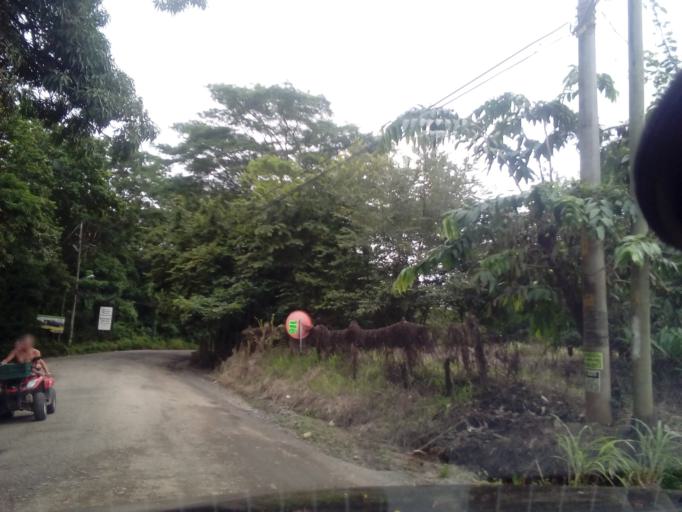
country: CR
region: Guanacaste
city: Samara
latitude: 9.9364
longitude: -85.6488
